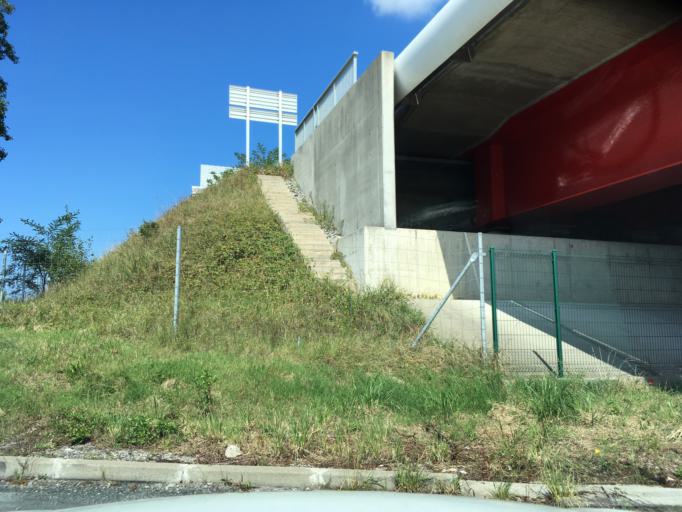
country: FR
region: Aquitaine
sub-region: Departement des Pyrenees-Atlantiques
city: Bayonne
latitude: 43.4870
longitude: -1.4489
